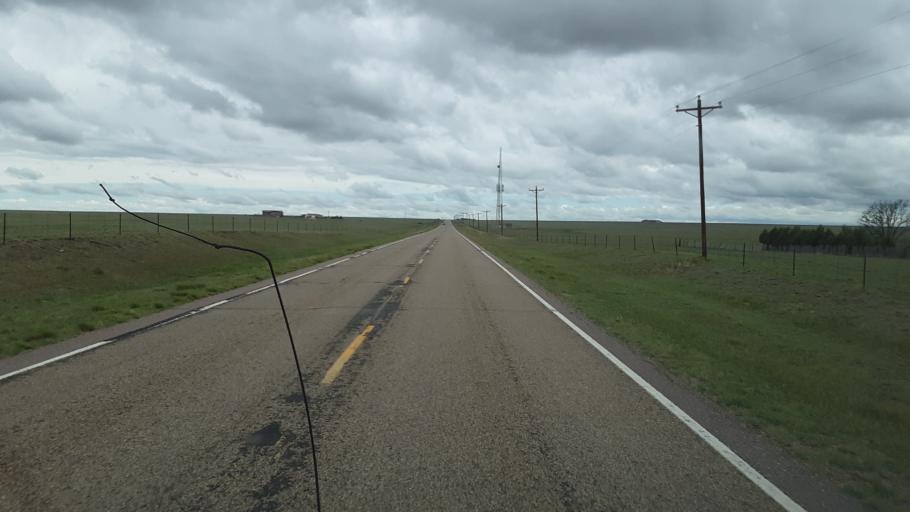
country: US
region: Colorado
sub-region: El Paso County
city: Ellicott
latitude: 38.8398
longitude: -104.0102
